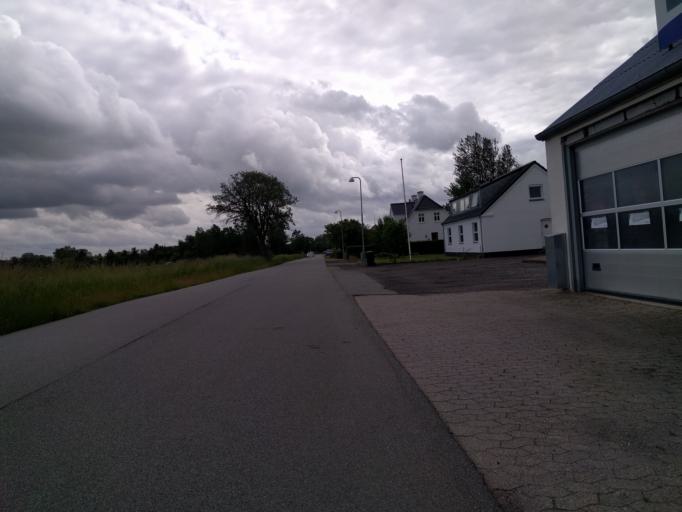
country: DK
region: South Denmark
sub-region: Kerteminde Kommune
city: Munkebo
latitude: 55.4431
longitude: 10.5197
